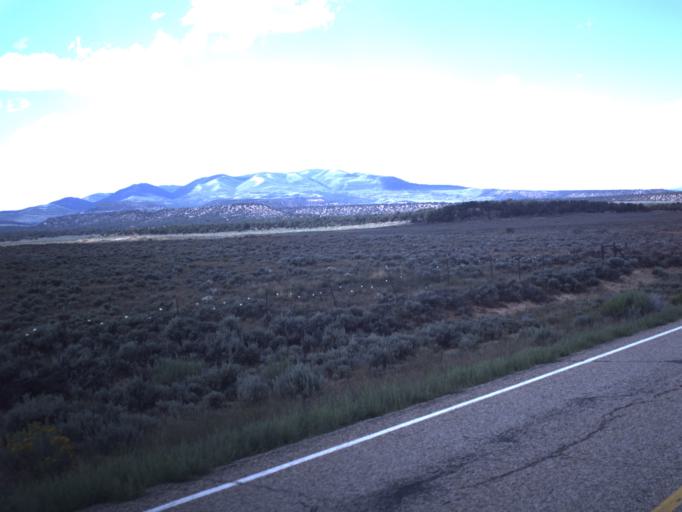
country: US
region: Utah
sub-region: Duchesne County
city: Duchesne
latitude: 40.2536
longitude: -110.7104
